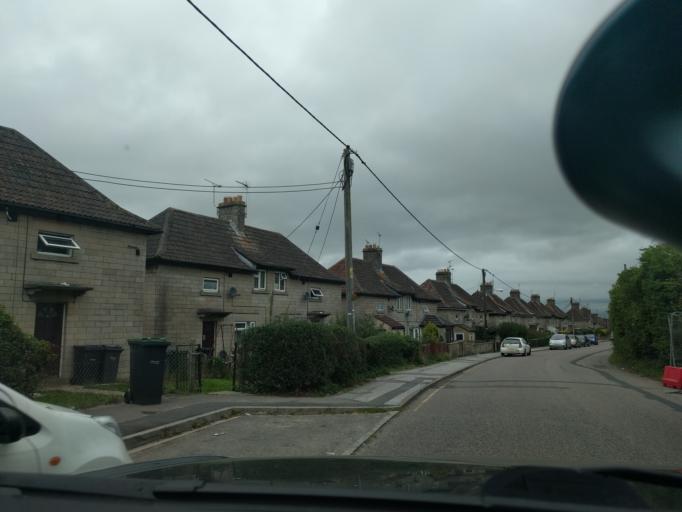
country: GB
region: England
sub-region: Wiltshire
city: Neston
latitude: 51.4229
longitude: -2.1972
